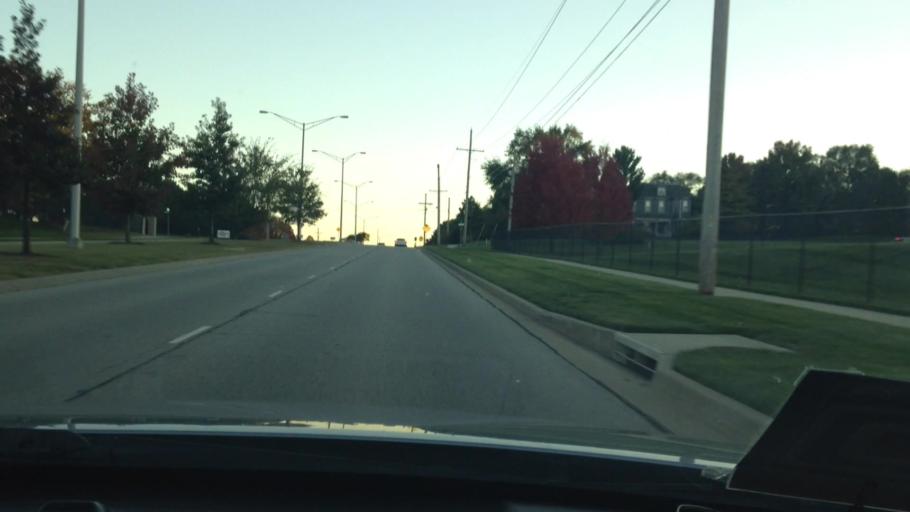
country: US
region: Kansas
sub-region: Johnson County
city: Lenexa
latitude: 38.8747
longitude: -94.7006
